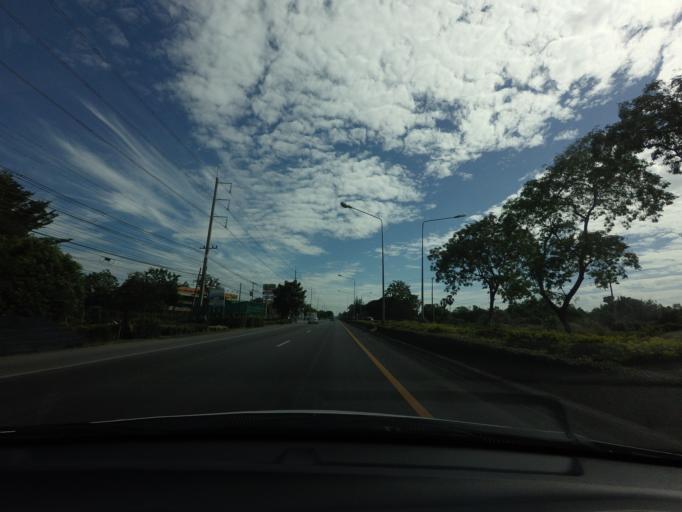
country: TH
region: Nakhon Nayok
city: Ongkharak
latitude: 14.0903
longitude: 100.9316
